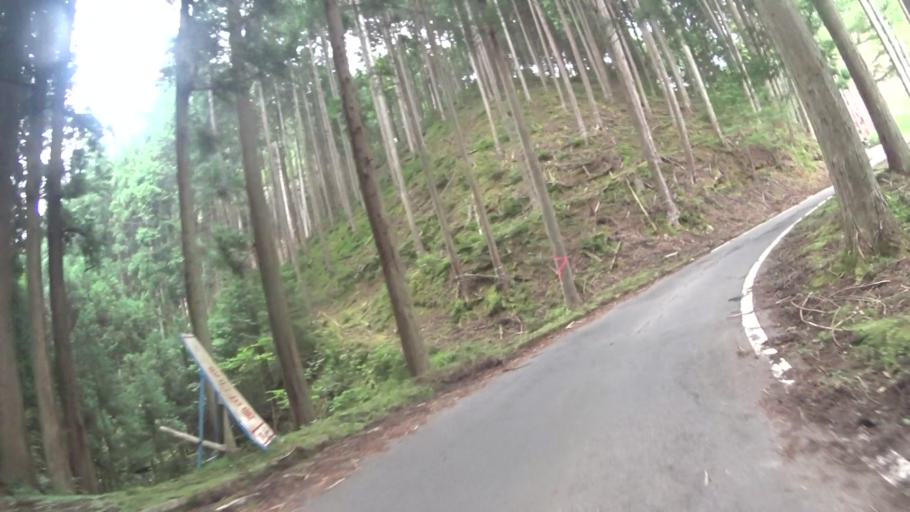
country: JP
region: Kyoto
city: Kameoka
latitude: 35.1685
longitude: 135.5718
